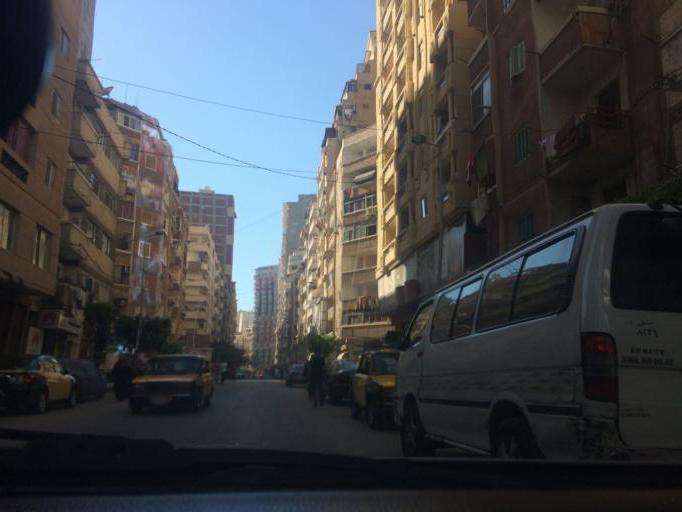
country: EG
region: Alexandria
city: Alexandria
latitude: 31.2602
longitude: 29.9957
